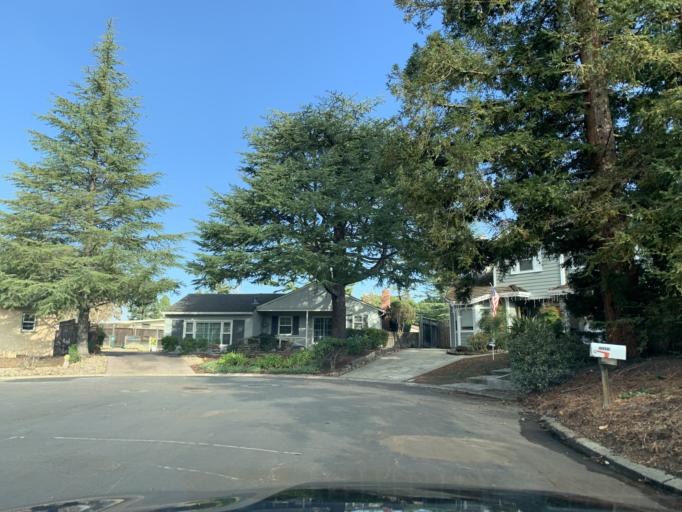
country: US
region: California
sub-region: Santa Clara County
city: Cupertino
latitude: 37.3355
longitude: -122.0611
